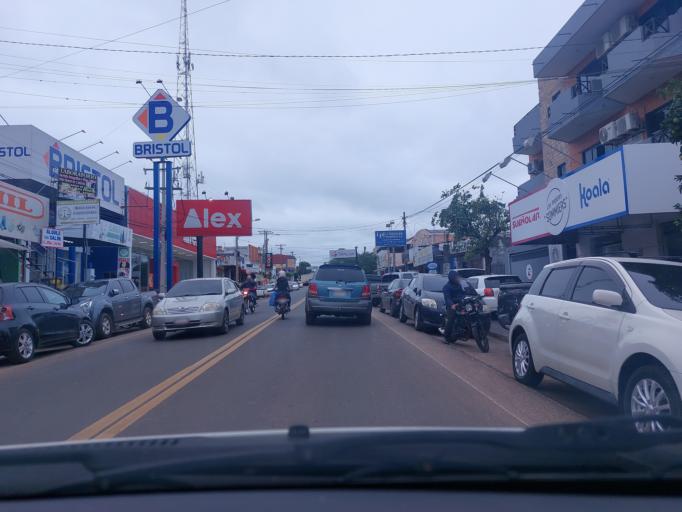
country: PY
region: San Pedro
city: Guayaybi
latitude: -24.6631
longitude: -56.4435
